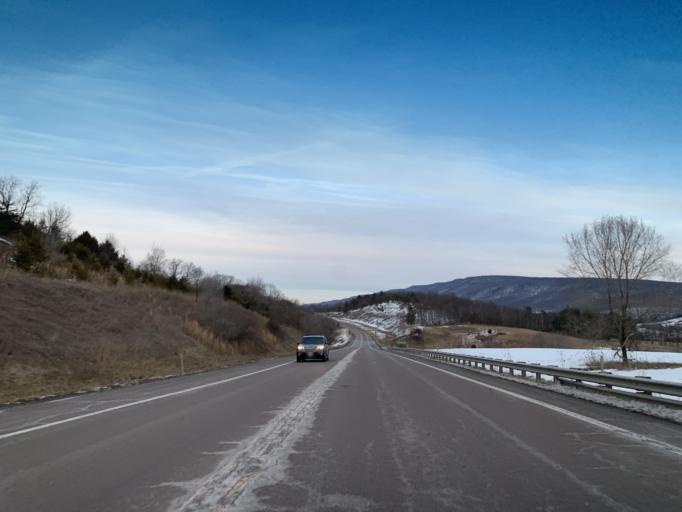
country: US
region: Maryland
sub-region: Allegany County
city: Cumberland
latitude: 39.6942
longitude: -78.7125
